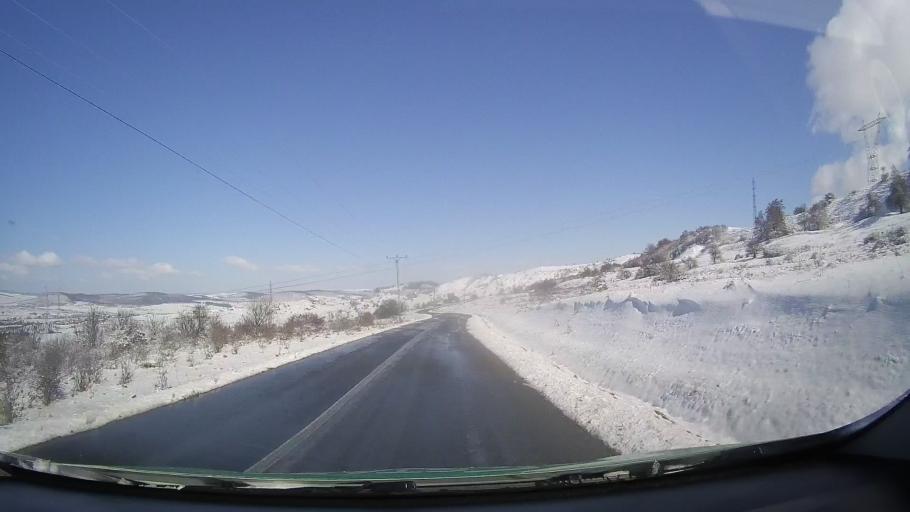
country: RO
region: Sibiu
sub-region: Comuna Avrig
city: Avrig
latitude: 45.7745
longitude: 24.3675
